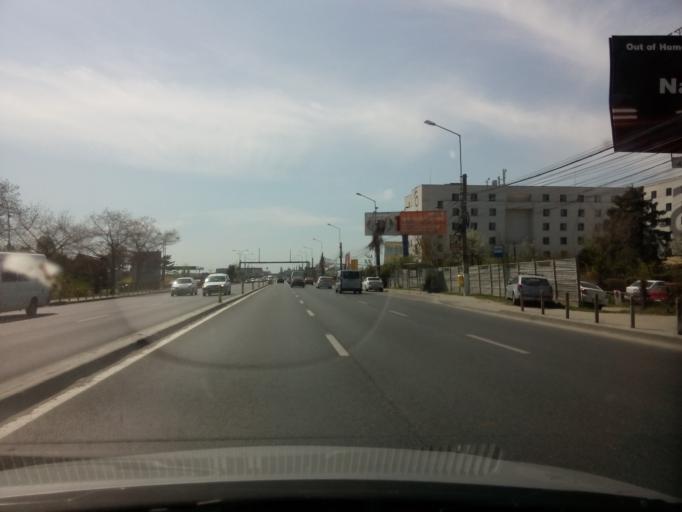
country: RO
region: Ilfov
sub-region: Comuna Otopeni
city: Otopeni
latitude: 44.5690
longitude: 26.0698
